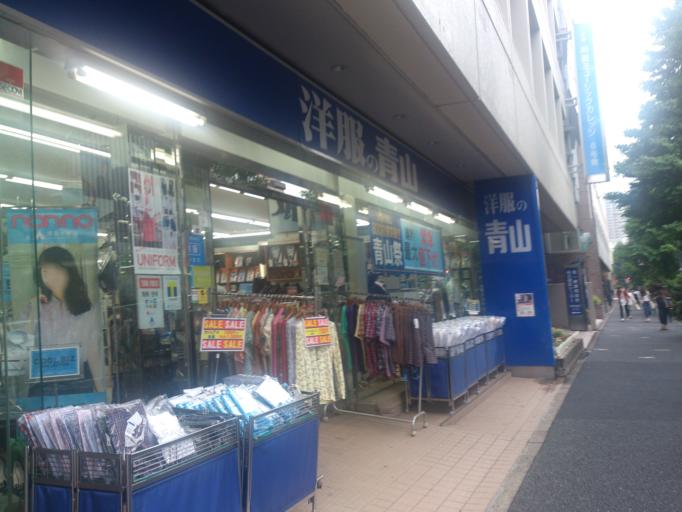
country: JP
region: Tokyo
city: Tokyo
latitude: 35.7013
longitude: 139.7554
